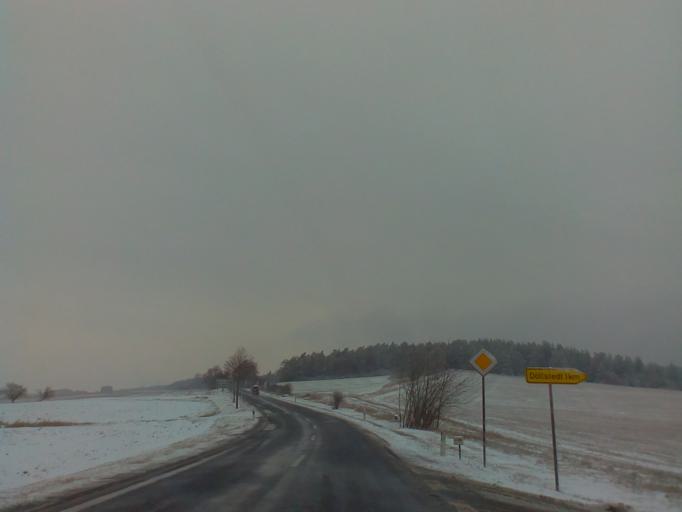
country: DE
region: Thuringia
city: Stadtilm
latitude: 50.7588
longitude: 11.1374
